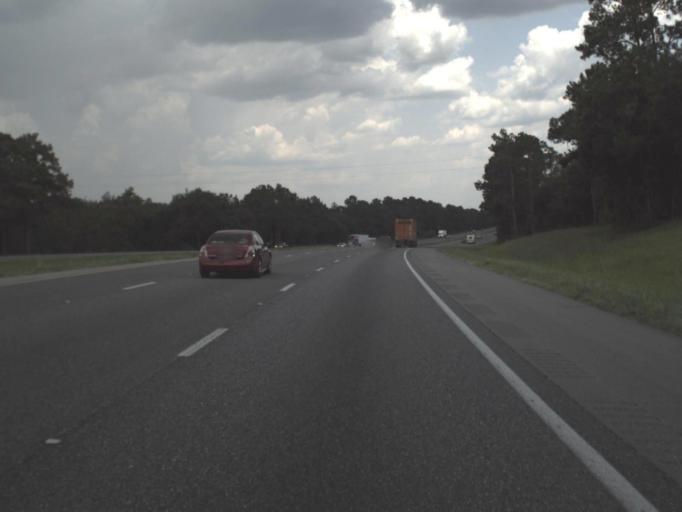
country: US
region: Florida
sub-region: Suwannee County
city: Wellborn
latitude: 30.3562
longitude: -82.8412
